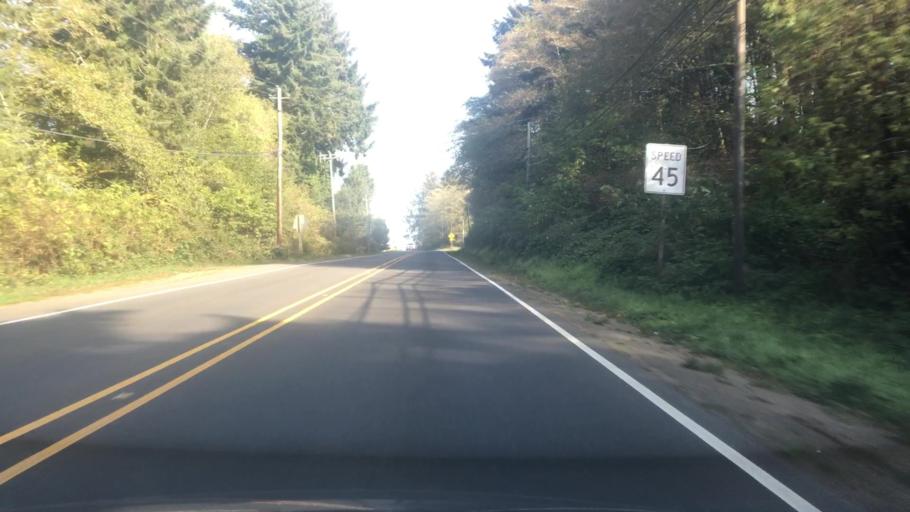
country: US
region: Oregon
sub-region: Lincoln County
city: Lincoln City
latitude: 44.9997
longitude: -123.9906
